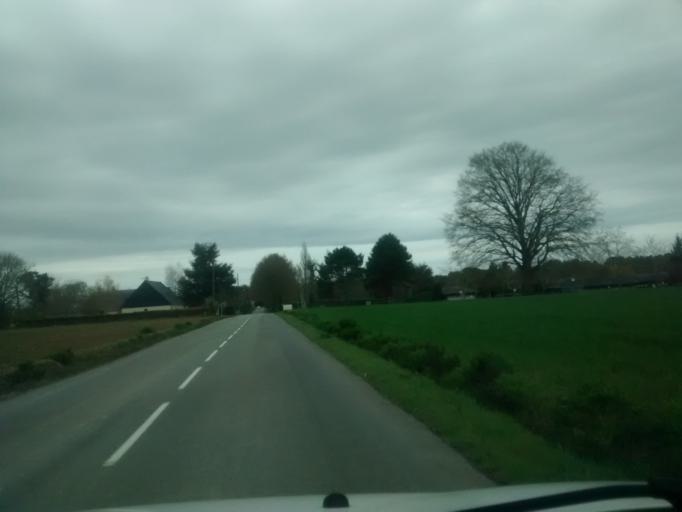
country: FR
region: Brittany
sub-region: Departement d'Ille-et-Vilaine
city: Fouillard
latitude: 48.1733
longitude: -1.6017
